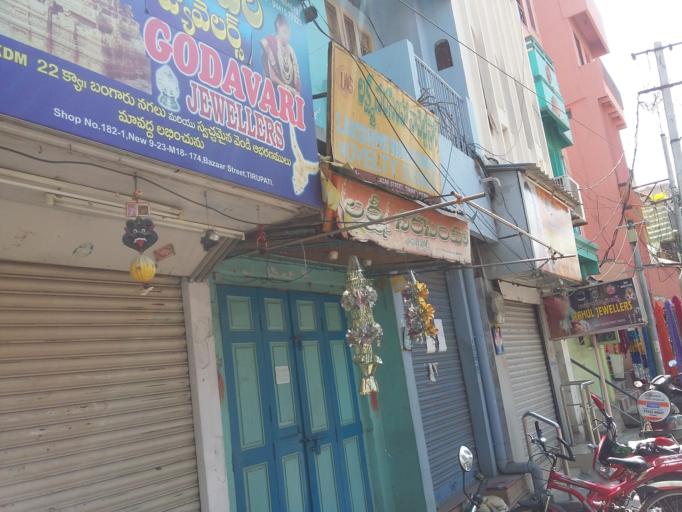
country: IN
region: Andhra Pradesh
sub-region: Chittoor
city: Tirupati
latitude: 13.6325
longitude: 79.4158
